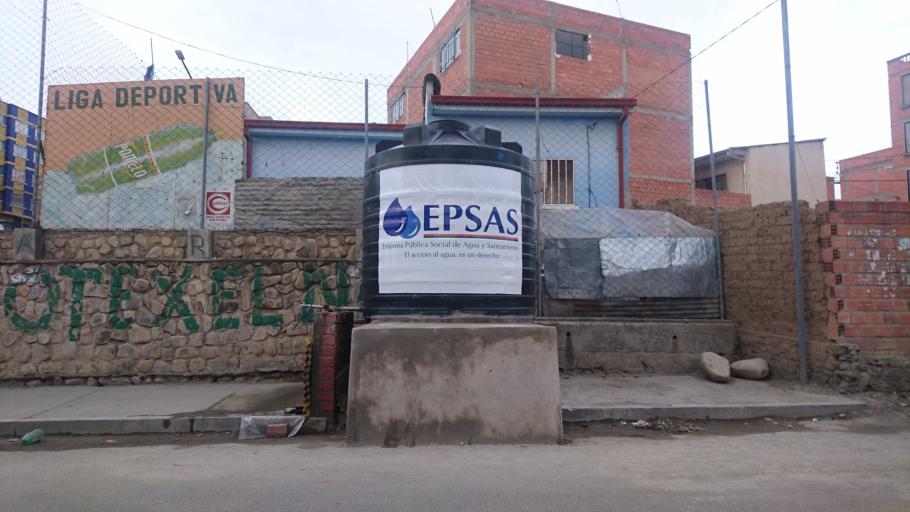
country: BO
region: La Paz
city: La Paz
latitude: -16.4909
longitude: -68.1045
